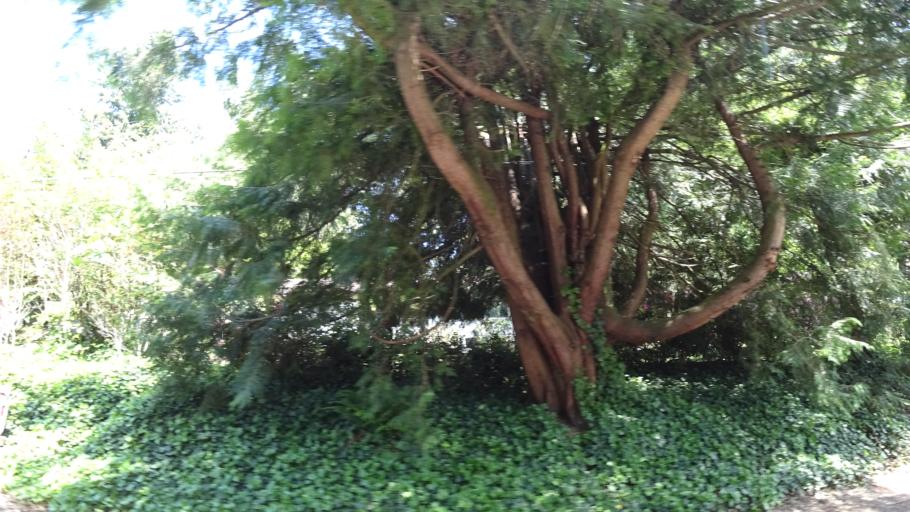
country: US
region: Oregon
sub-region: Washington County
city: Metzger
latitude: 45.4498
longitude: -122.7317
